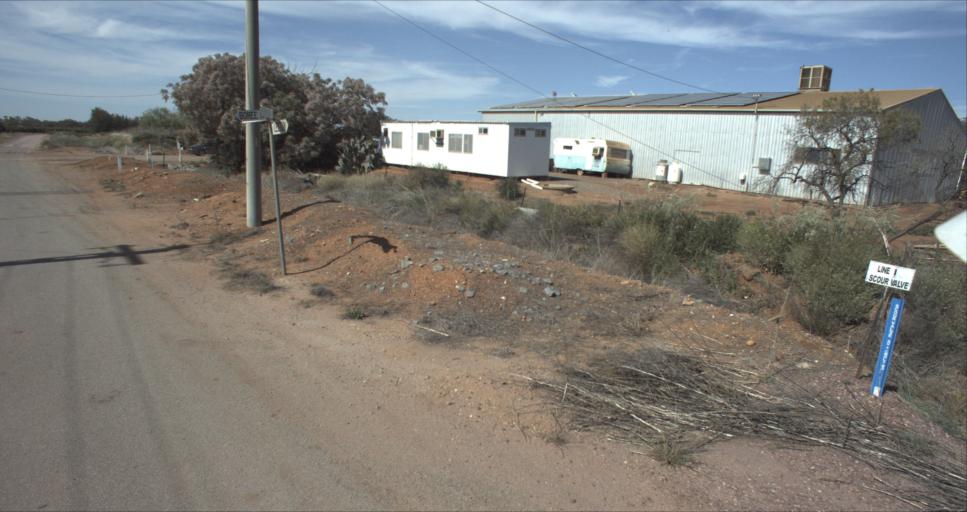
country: AU
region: New South Wales
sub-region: Leeton
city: Leeton
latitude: -34.5807
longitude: 146.4882
